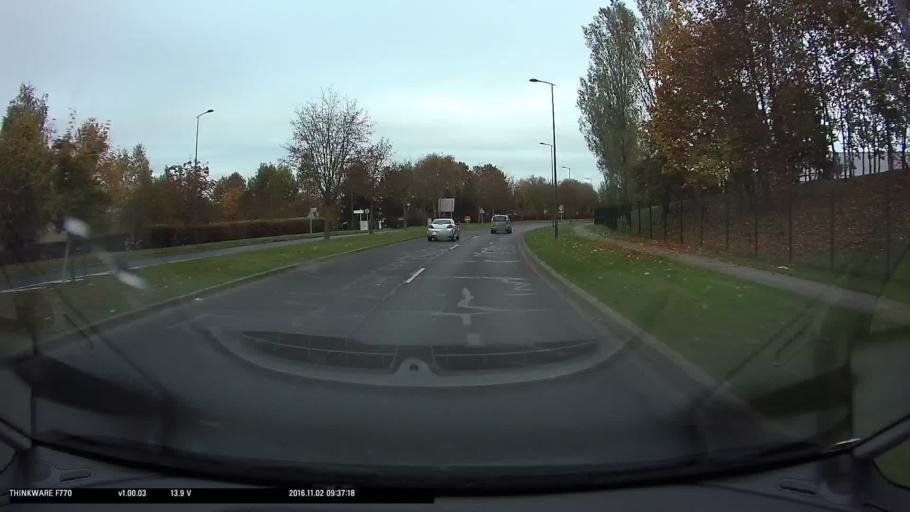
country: FR
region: Ile-de-France
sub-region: Departement du Val-d'Oise
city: Vaureal
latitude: 49.0547
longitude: 2.0247
